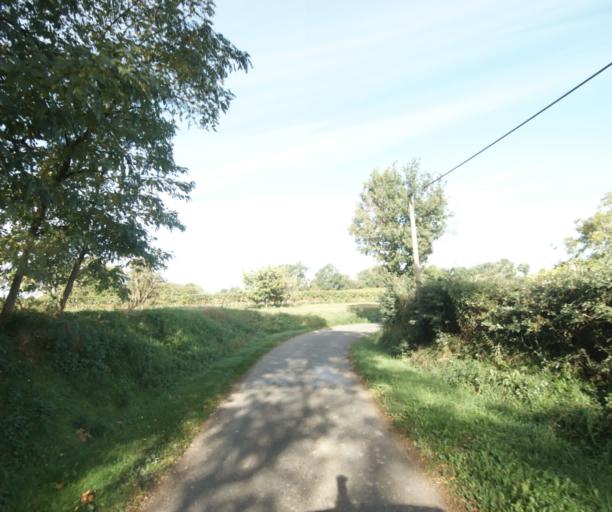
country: FR
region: Midi-Pyrenees
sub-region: Departement du Gers
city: Eauze
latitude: 43.8871
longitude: 0.1338
